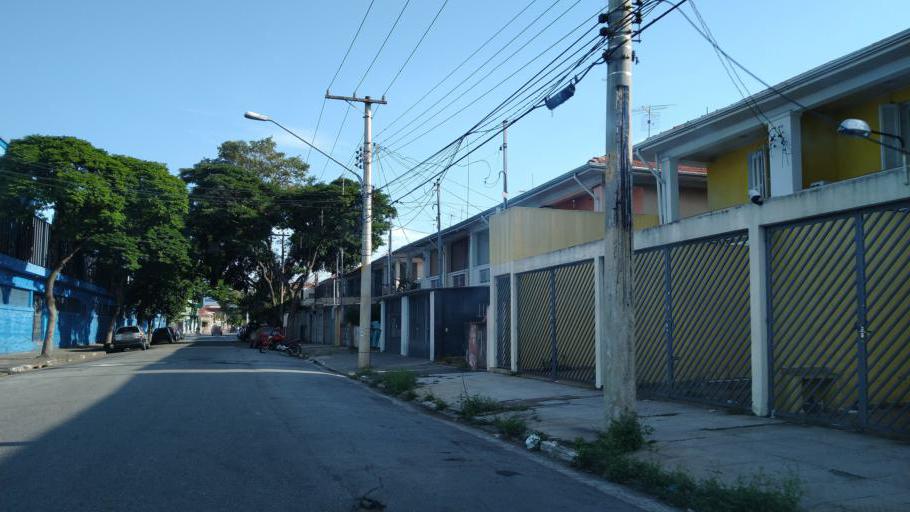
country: BR
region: Sao Paulo
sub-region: Sao Paulo
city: Sao Paulo
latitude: -23.5243
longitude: -46.6130
